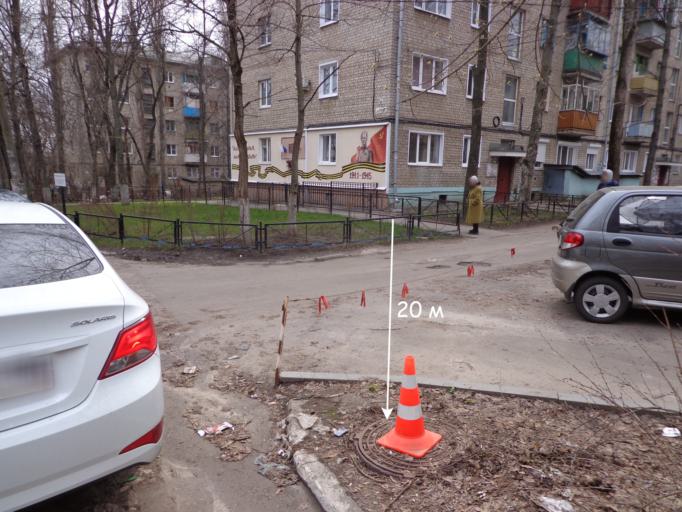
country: RU
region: Voronezj
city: Voronezh
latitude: 51.7005
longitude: 39.2287
